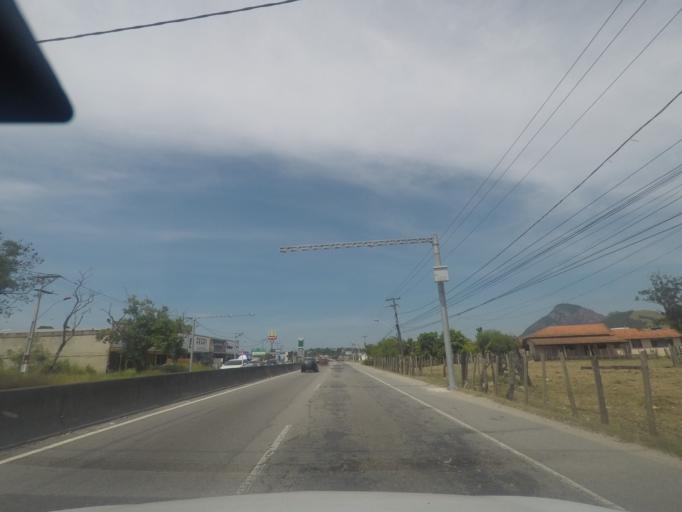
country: BR
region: Rio de Janeiro
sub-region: Marica
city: Marica
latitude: -22.9274
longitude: -42.8678
